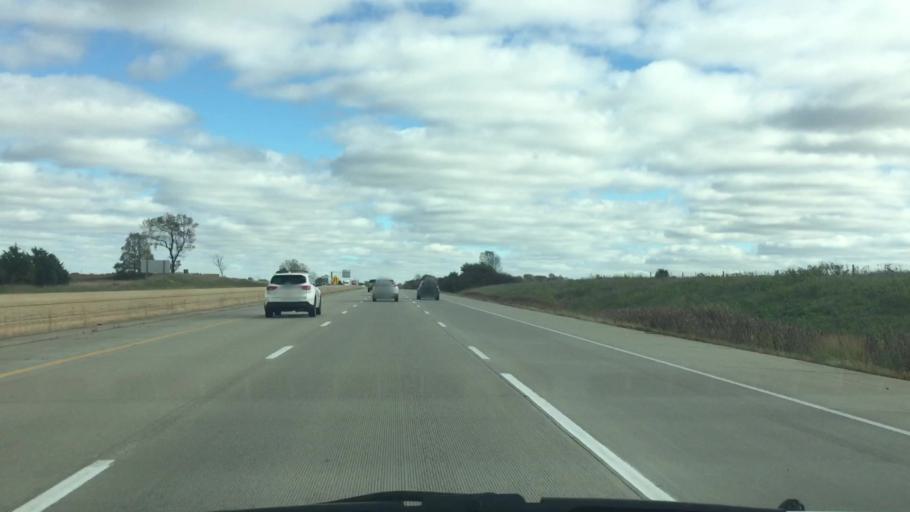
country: US
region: Iowa
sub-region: Johnson County
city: Iowa City
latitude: 41.6844
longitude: -91.4804
